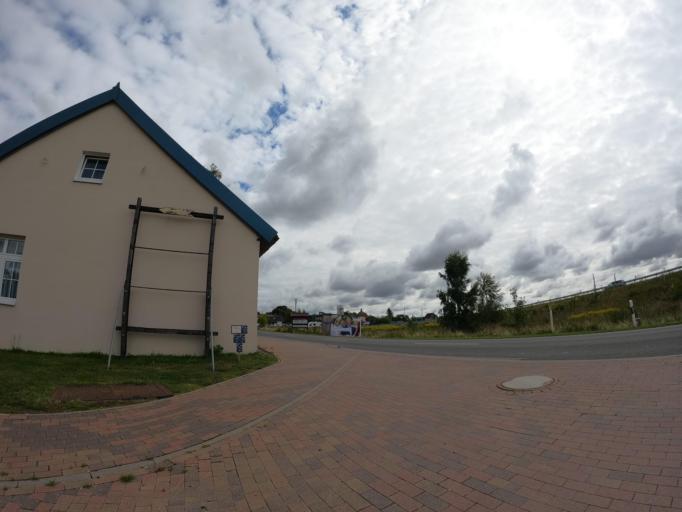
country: DE
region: Mecklenburg-Vorpommern
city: Rambin
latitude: 54.3534
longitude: 13.1979
